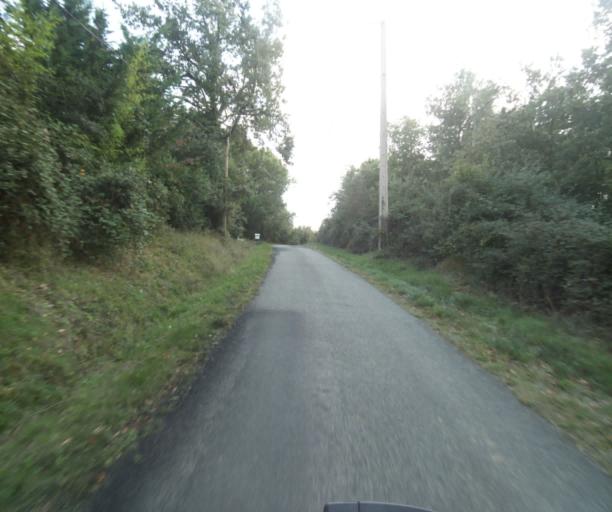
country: FR
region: Midi-Pyrenees
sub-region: Departement de la Haute-Garonne
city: Launac
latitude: 43.8130
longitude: 1.1316
